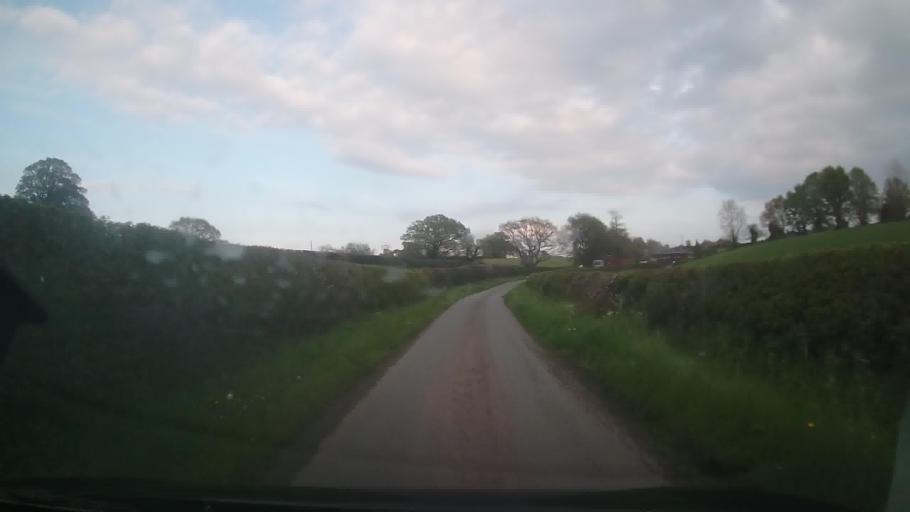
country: GB
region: England
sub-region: Shropshire
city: Ellesmere
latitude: 52.9301
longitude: -2.8355
